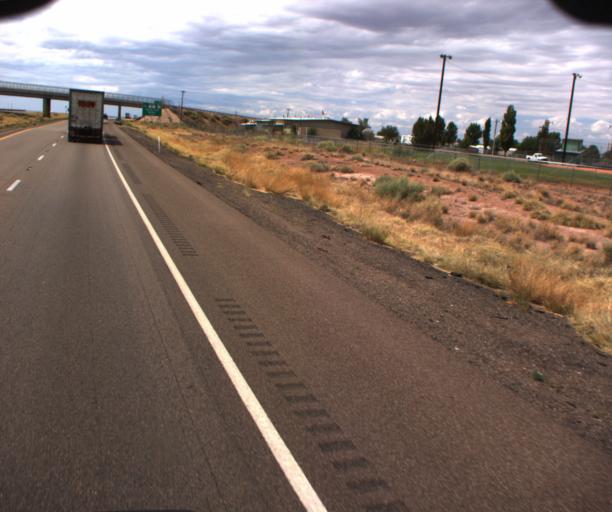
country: US
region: Arizona
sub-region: Navajo County
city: Holbrook
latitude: 34.9255
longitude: -110.1362
